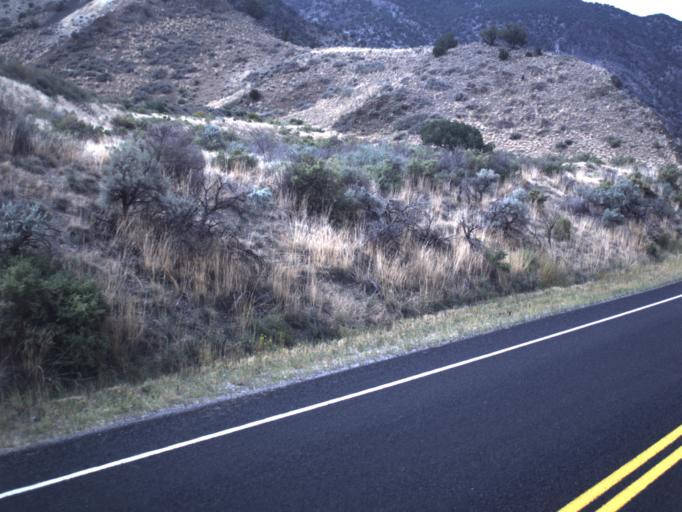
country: US
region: Utah
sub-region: Sevier County
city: Monroe
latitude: 38.5236
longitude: -112.2654
